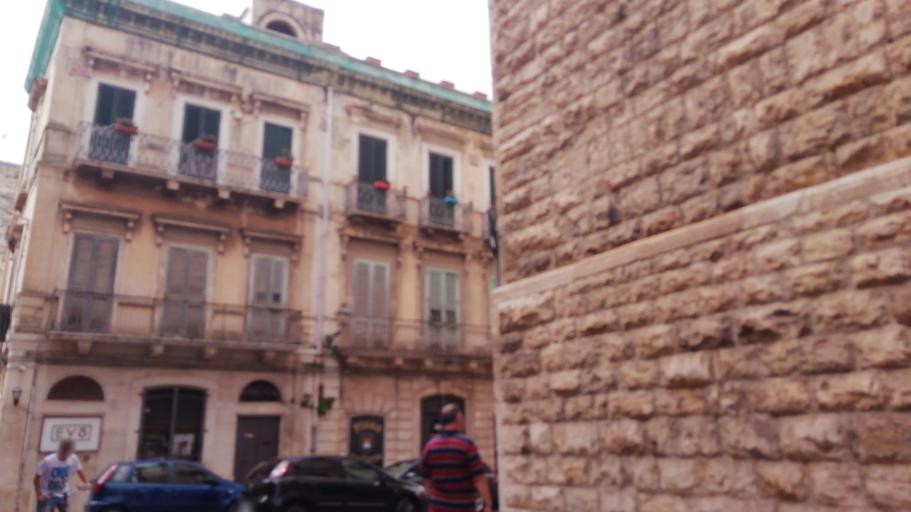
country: IT
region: Apulia
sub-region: Provincia di Barletta - Andria - Trani
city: Andria
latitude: 41.2252
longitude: 16.2968
